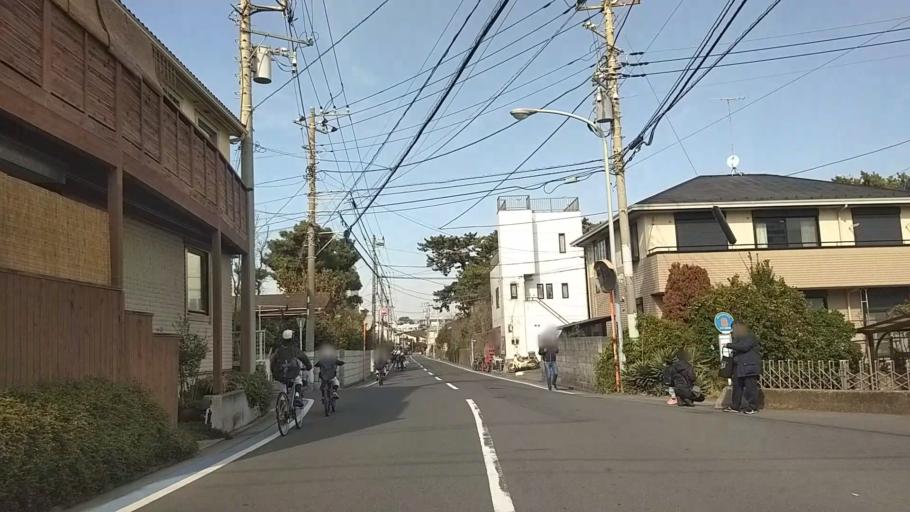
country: JP
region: Kanagawa
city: Chigasaki
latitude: 35.3196
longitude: 139.3997
